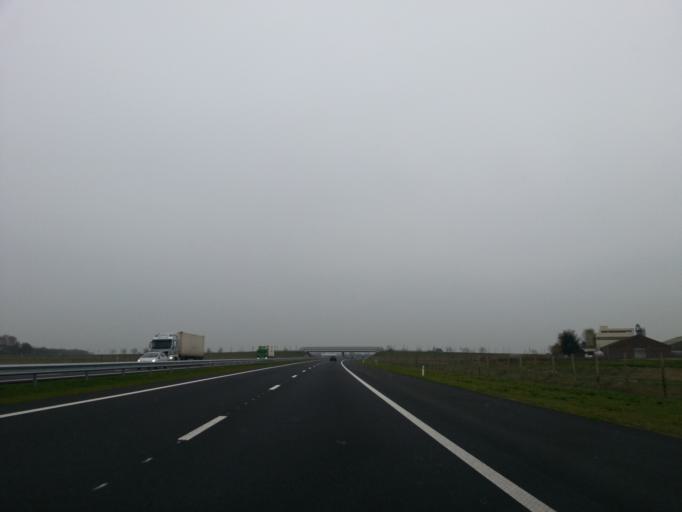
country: NL
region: North Brabant
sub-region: Gemeente Steenbergen
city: Steenbergen
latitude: 51.5989
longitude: 4.3333
